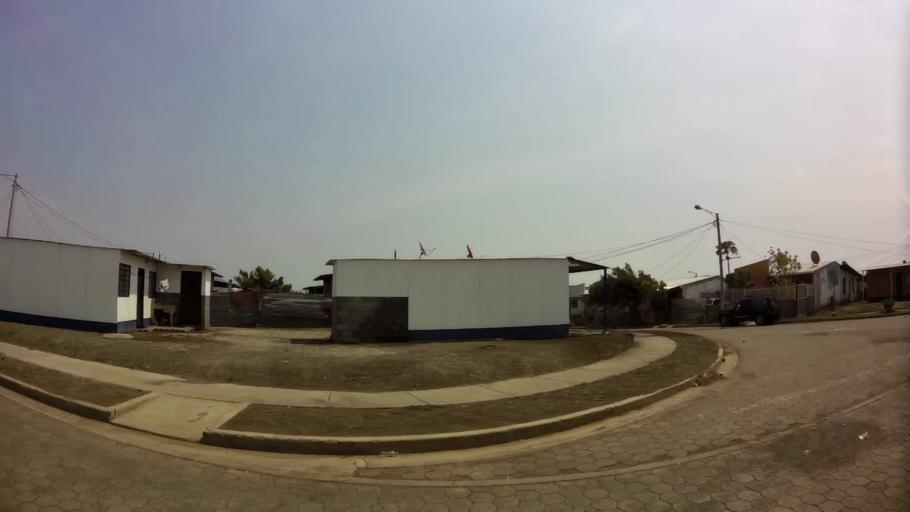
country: NI
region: Managua
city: Ciudad Sandino
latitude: 12.1605
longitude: -86.3124
